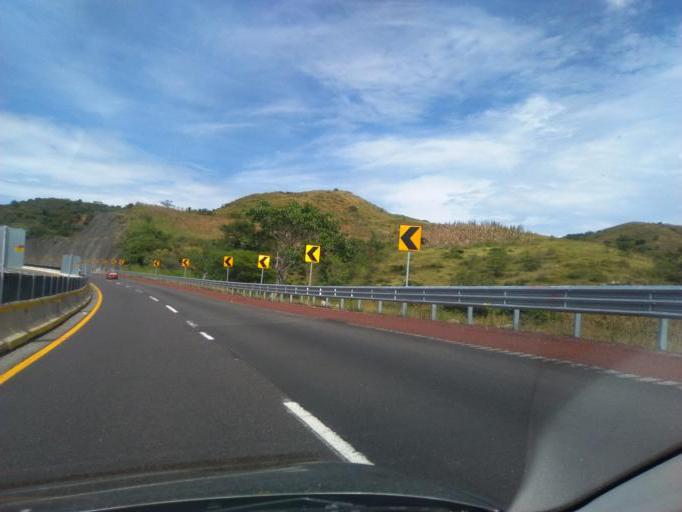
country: MX
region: Guerrero
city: Mazatlan
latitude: 17.4016
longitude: -99.4616
